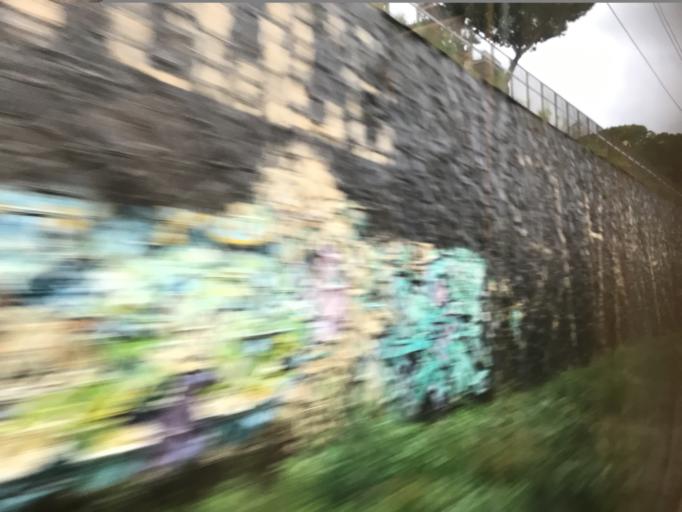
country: IT
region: Latium
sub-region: Citta metropolitana di Roma Capitale
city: Vitinia
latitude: 41.8347
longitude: 12.4271
